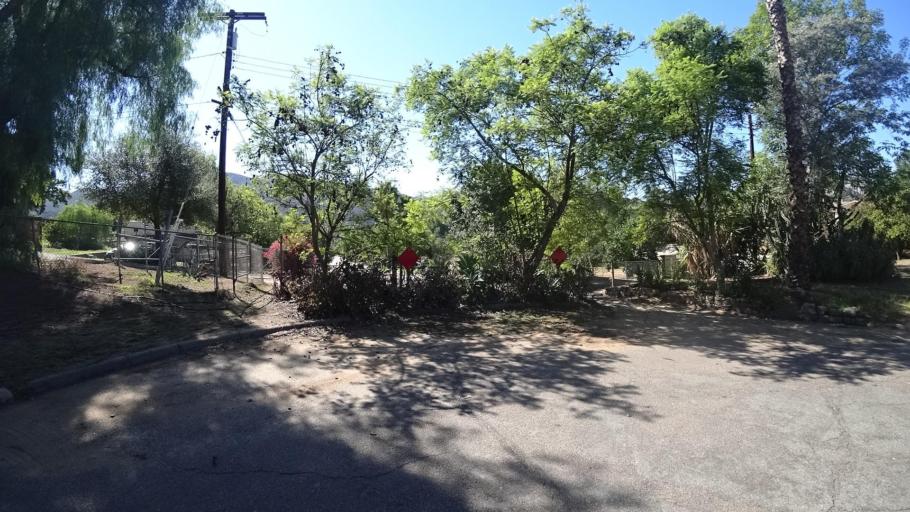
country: US
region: California
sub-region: San Diego County
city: Rancho San Diego
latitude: 32.7294
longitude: -116.9137
